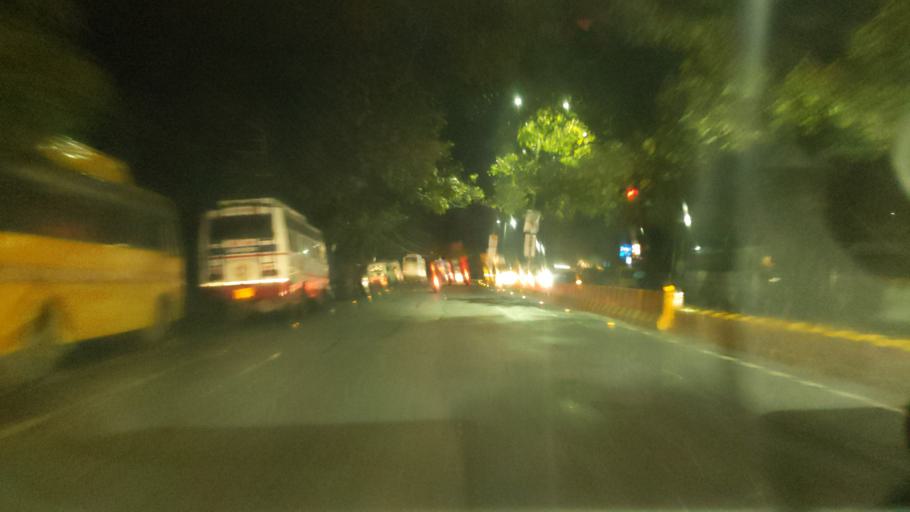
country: IN
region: Uttarakhand
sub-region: Naini Tal
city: Haldwani
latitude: 29.2574
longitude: 79.5429
